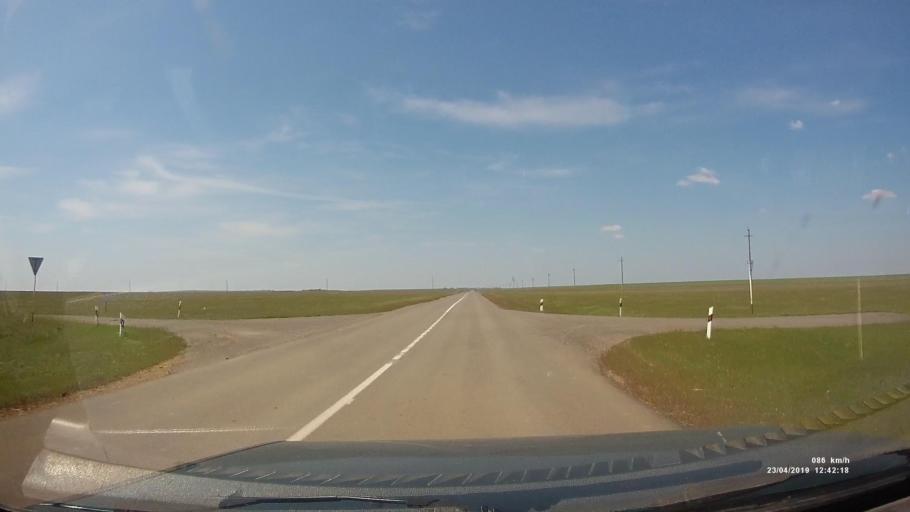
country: RU
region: Kalmykiya
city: Yashalta
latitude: 46.4548
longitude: 42.6678
